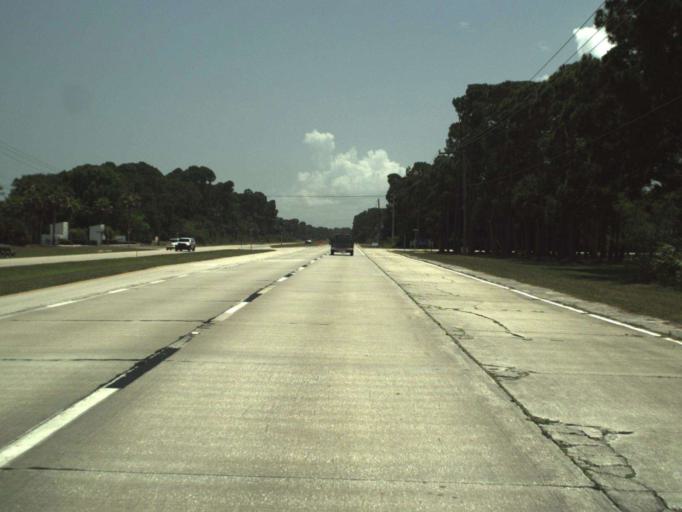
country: US
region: Florida
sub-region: Volusia County
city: Oak Hill
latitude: 28.9223
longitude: -80.8729
